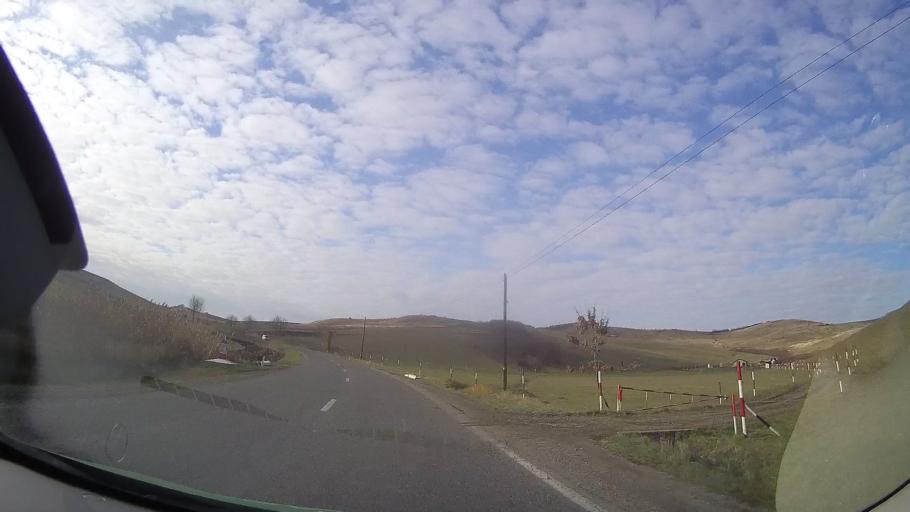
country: RO
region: Cluj
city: Jucu Herghelia
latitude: 46.8119
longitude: 23.7992
